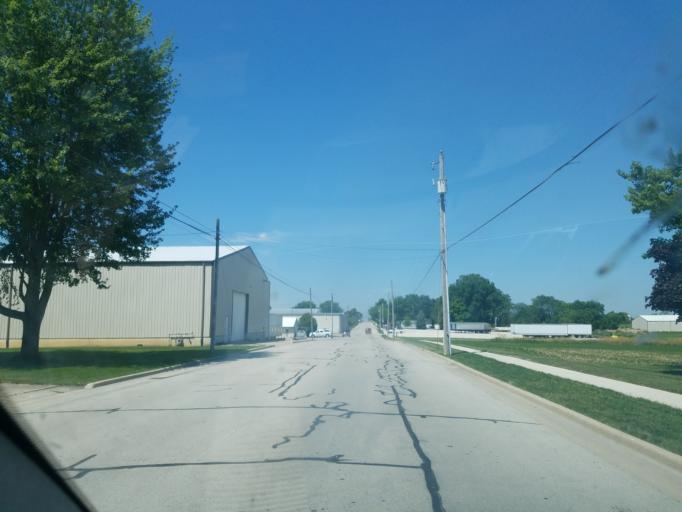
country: US
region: Ohio
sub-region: Mercer County
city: Saint Henry
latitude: 40.4214
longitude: -84.6408
